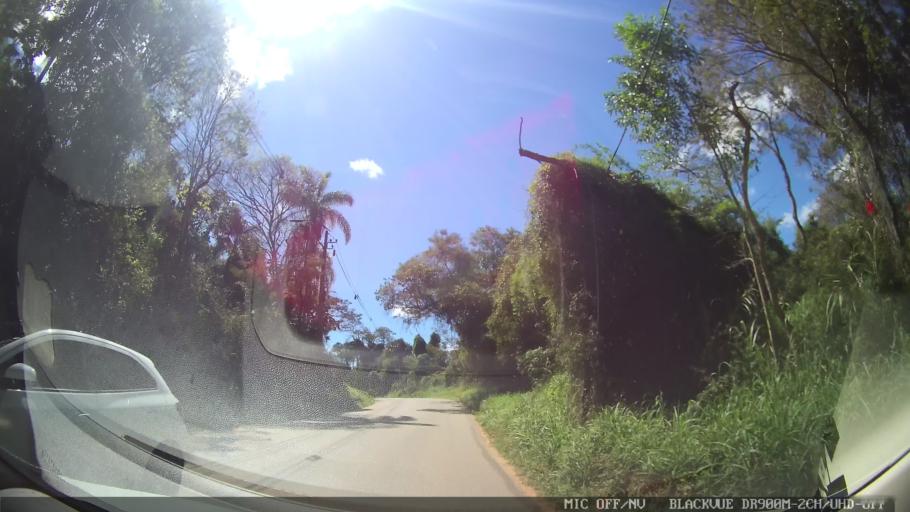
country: BR
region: Sao Paulo
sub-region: Campo Limpo Paulista
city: Campo Limpo Paulista
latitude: -23.1676
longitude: -46.7338
